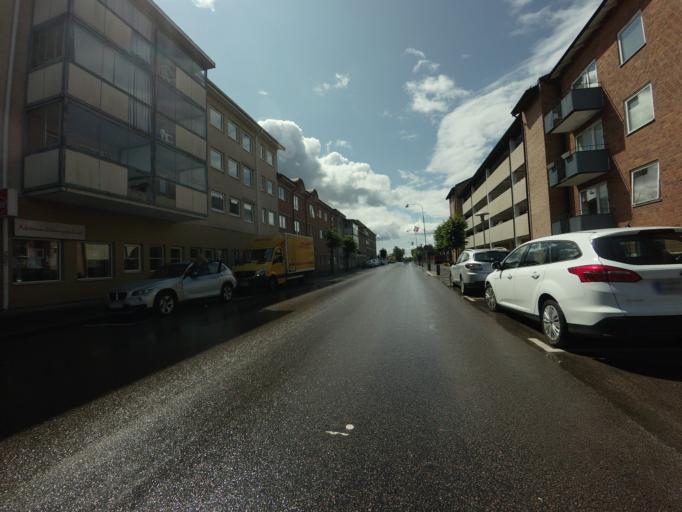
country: SE
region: Skane
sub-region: Osby Kommun
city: Osby
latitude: 56.3802
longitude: 13.9924
